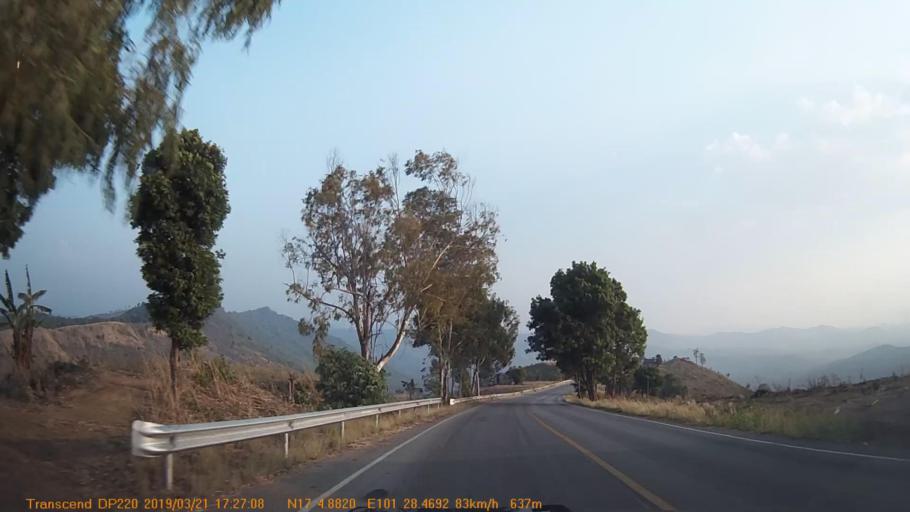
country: TH
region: Loei
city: Phu Luang
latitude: 17.0810
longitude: 101.4745
